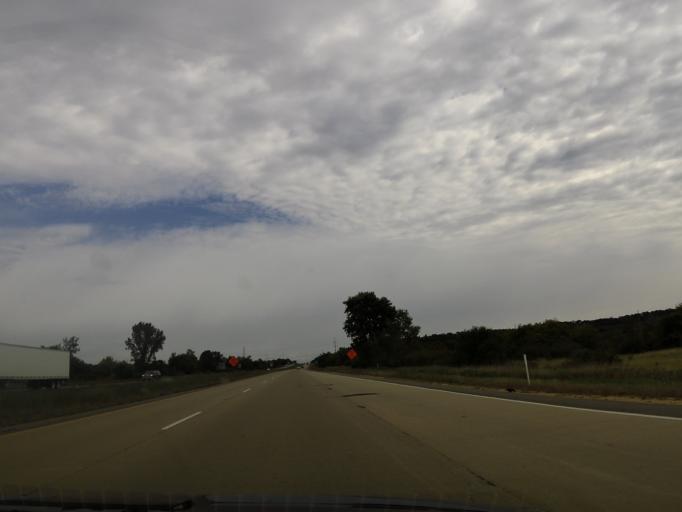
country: US
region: Wisconsin
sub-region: Monroe County
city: Tomah
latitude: 43.9596
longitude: -90.4998
